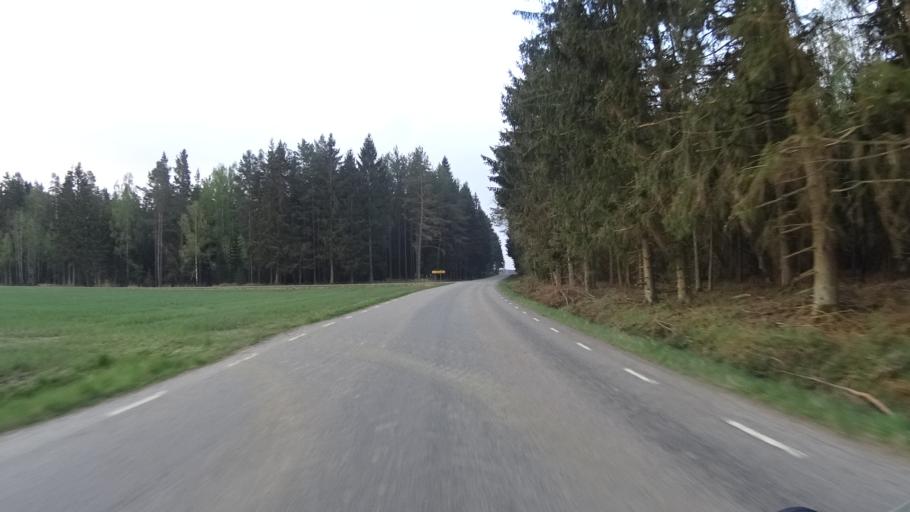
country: SE
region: Vaestra Goetaland
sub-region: Gotene Kommun
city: Kallby
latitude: 58.4586
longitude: 13.3375
